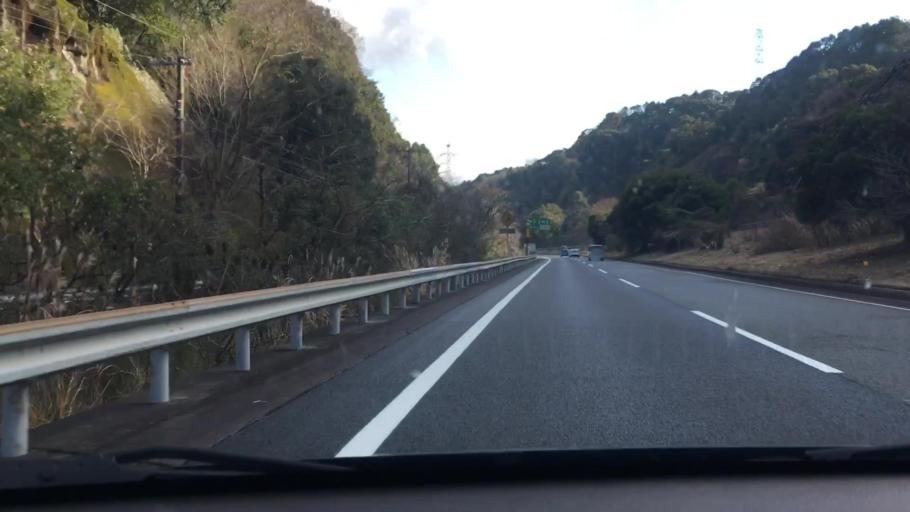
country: JP
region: Kumamoto
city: Hitoyoshi
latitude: 32.2708
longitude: 130.7600
